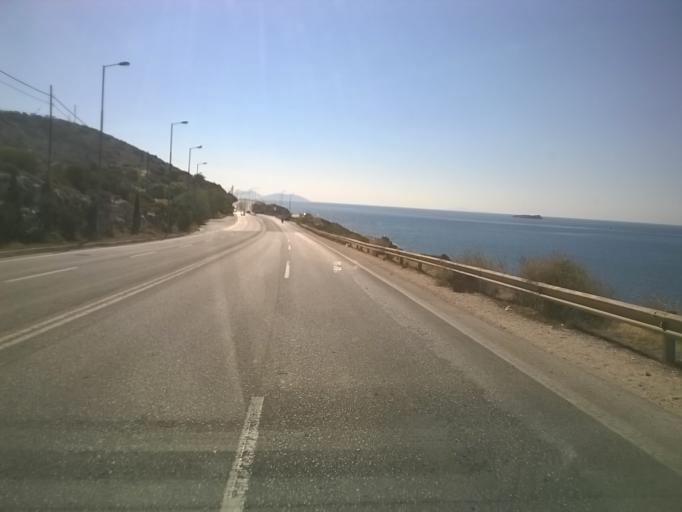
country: GR
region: Attica
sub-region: Nomarchia Anatolikis Attikis
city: Vari
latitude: 37.8171
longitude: 23.8195
